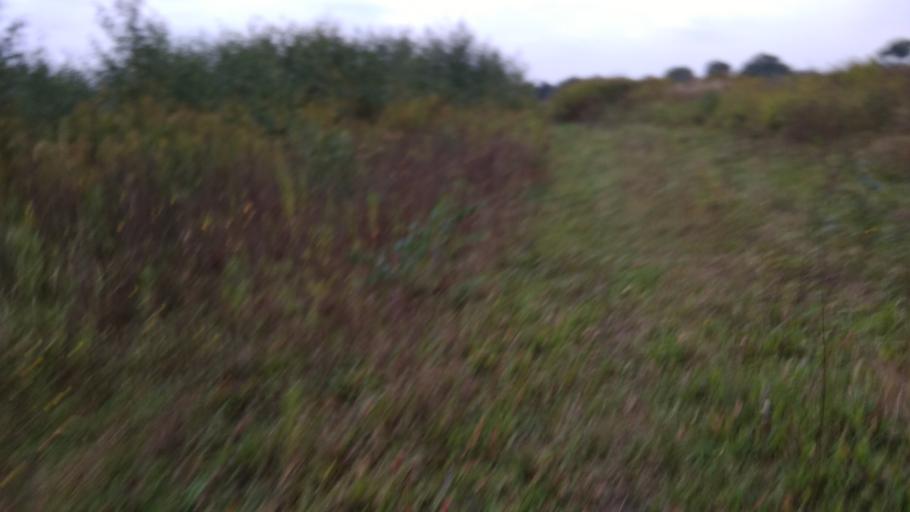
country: PL
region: Kujawsko-Pomorskie
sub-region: Bydgoszcz
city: Fordon
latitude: 53.2104
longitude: 18.1467
